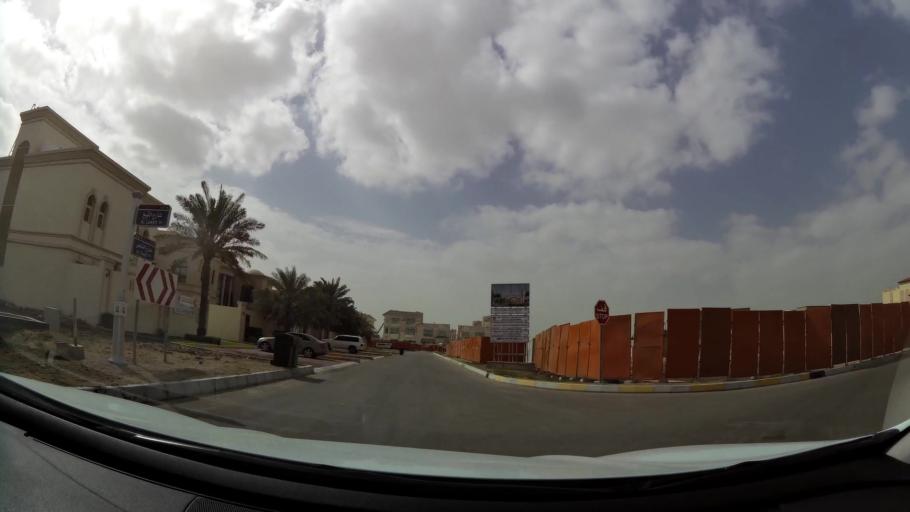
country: AE
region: Abu Dhabi
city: Abu Dhabi
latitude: 24.4069
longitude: 54.4937
